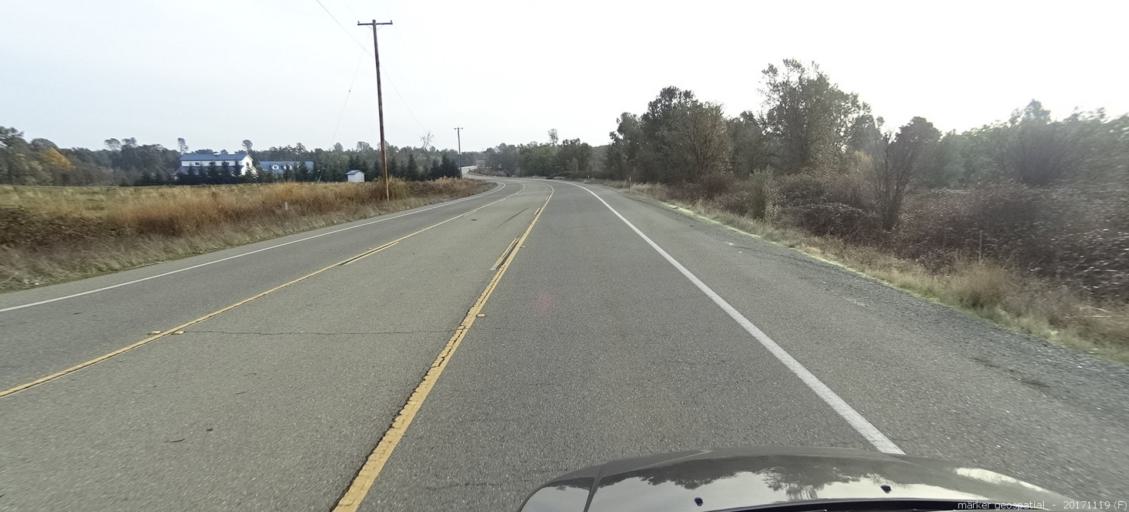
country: US
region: California
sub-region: Shasta County
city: Anderson
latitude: 40.5083
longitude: -122.3215
